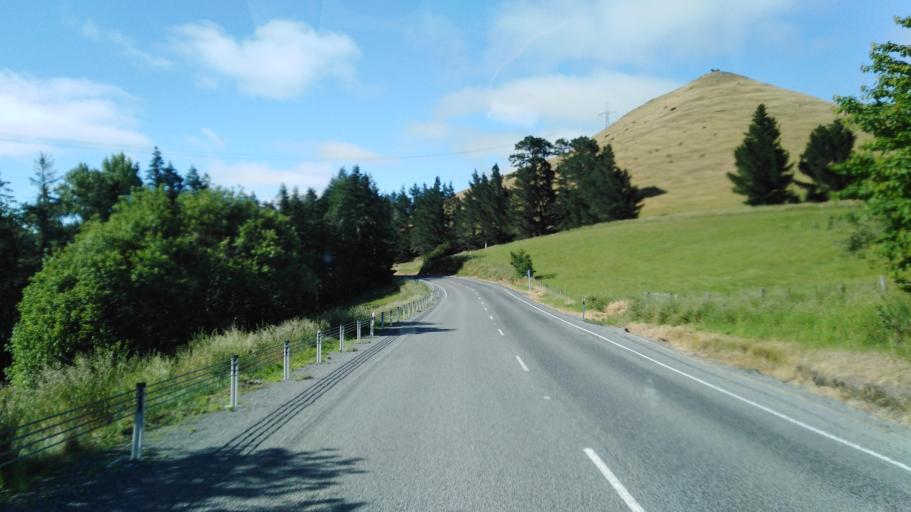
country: NZ
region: Canterbury
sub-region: Hurunui District
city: Amberley
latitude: -43.0125
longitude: 172.7024
